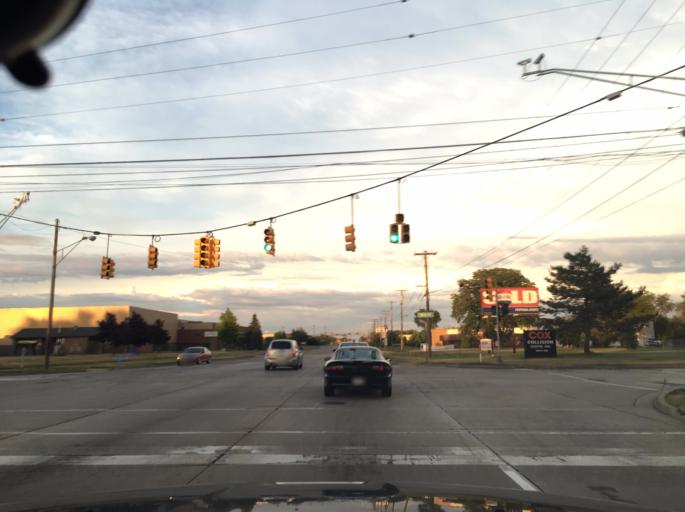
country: US
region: Michigan
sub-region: Macomb County
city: Fraser
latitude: 42.5540
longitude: -82.9307
